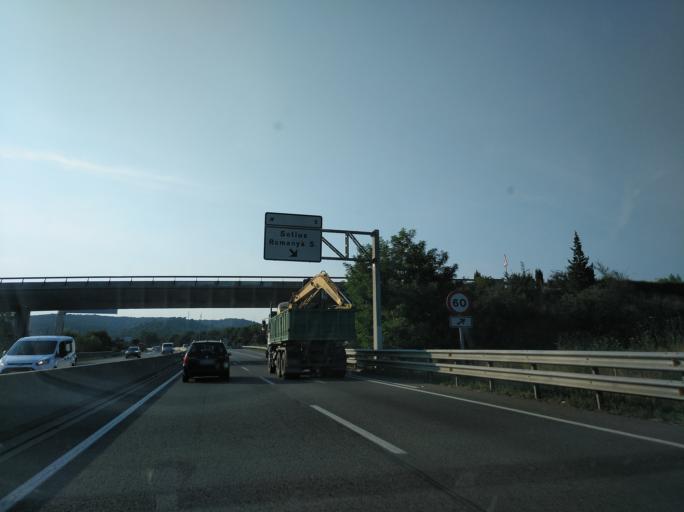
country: ES
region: Catalonia
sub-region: Provincia de Girona
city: Santa Cristina d'Aro
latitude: 41.8222
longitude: 2.9768
